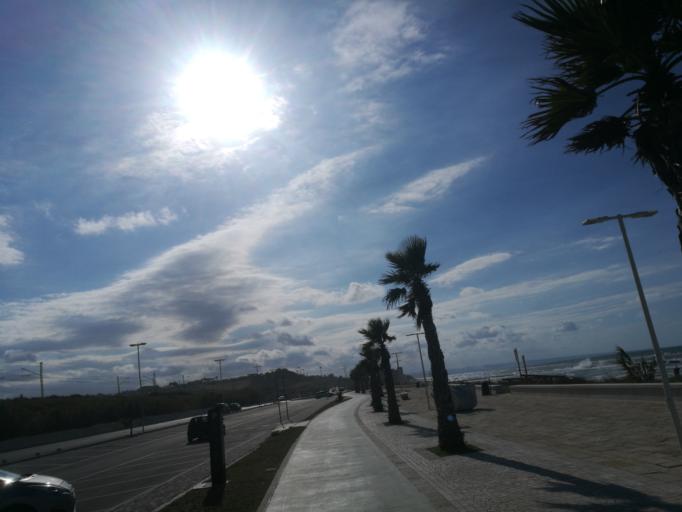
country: IT
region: Molise
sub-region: Provincia di Campobasso
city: Termoli
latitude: 42.0078
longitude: 14.9671
